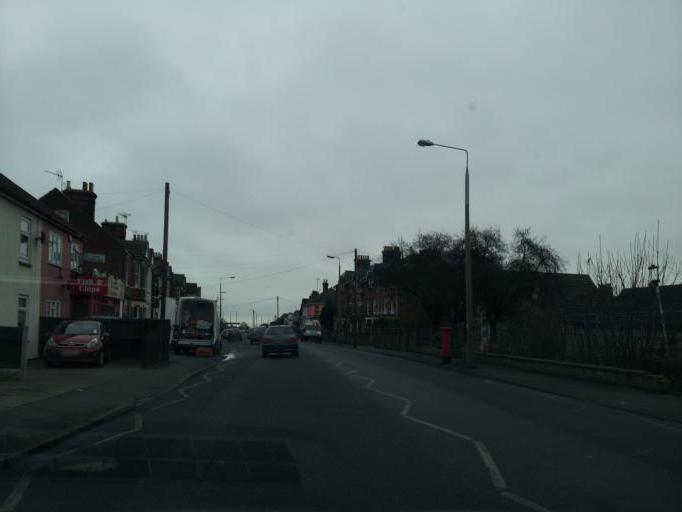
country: GB
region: England
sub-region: Essex
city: Dovercourt
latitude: 51.9347
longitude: 1.2627
